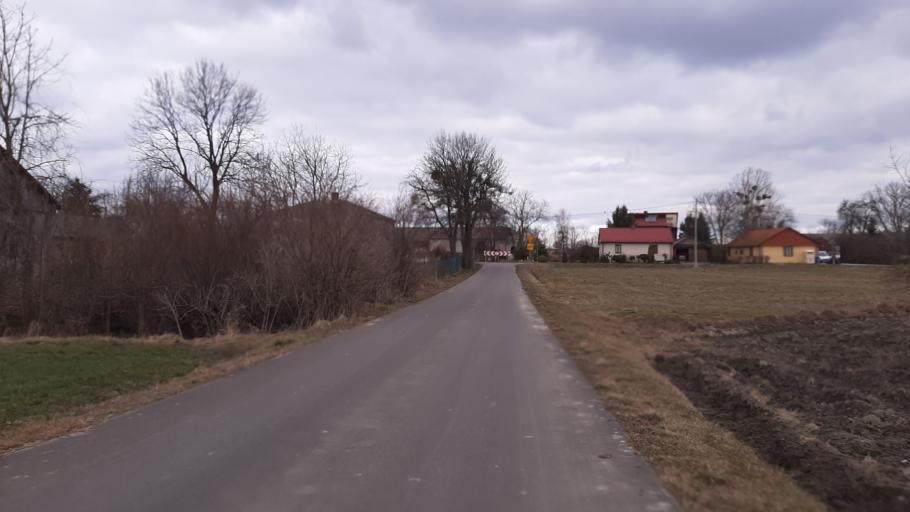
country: PL
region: Lublin Voivodeship
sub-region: Powiat lubelski
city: Garbow
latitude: 51.3521
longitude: 22.3932
